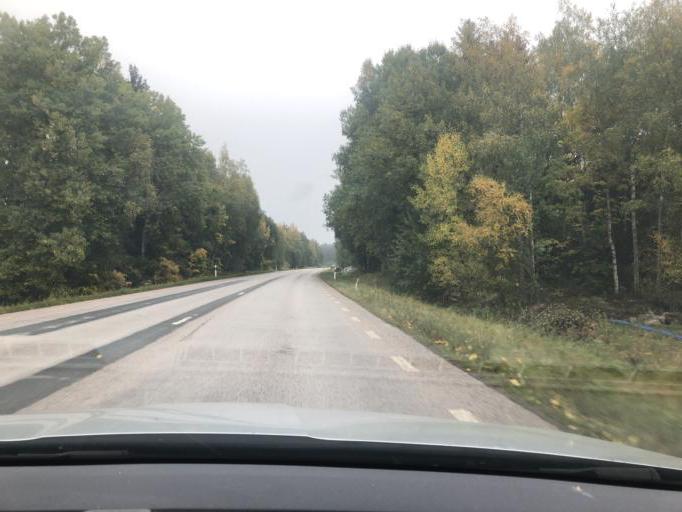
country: SE
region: Uppsala
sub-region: Tierps Kommun
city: Orbyhus
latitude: 60.2163
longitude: 17.7303
